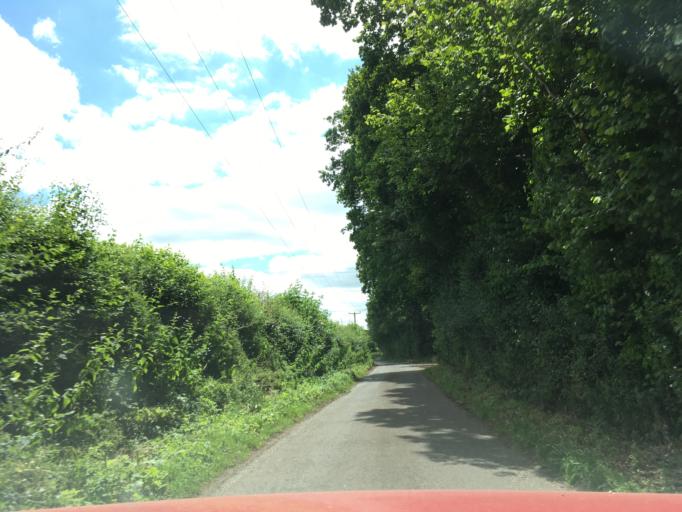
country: GB
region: England
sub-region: Hampshire
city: Highclere
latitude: 51.2882
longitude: -1.4178
